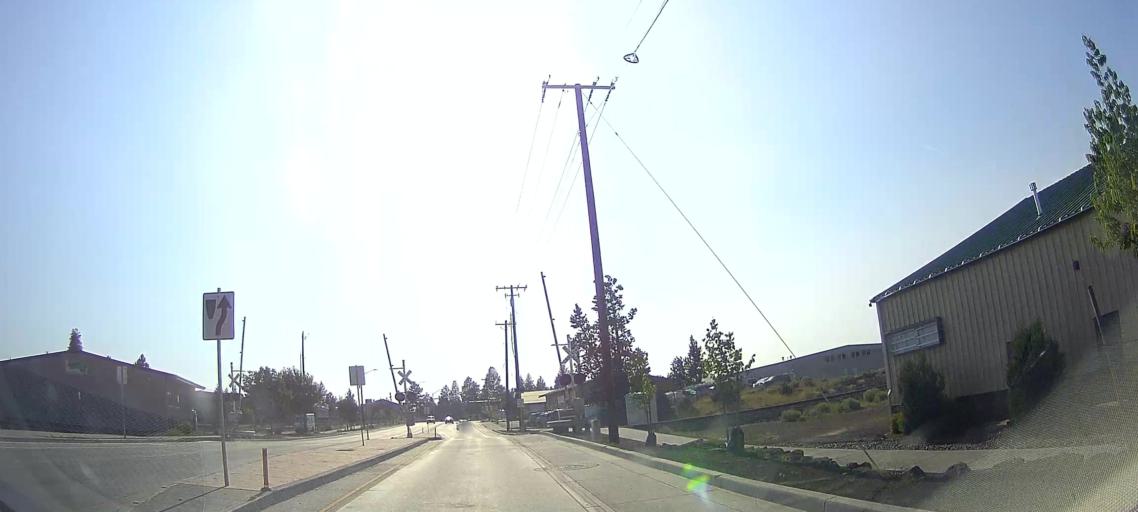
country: US
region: Oregon
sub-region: Deschutes County
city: Bend
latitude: 44.0370
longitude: -121.2887
